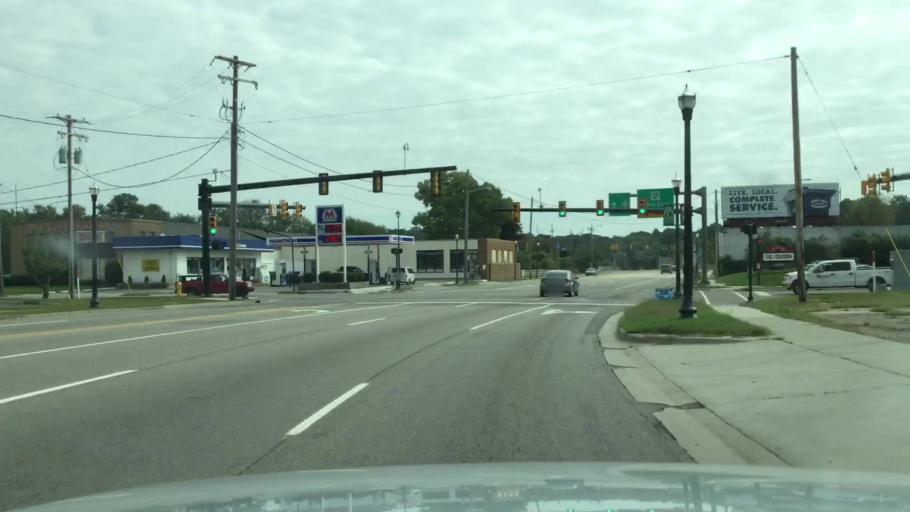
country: US
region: Michigan
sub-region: Kalamazoo County
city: Kalamazoo
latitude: 42.2946
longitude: -85.5753
